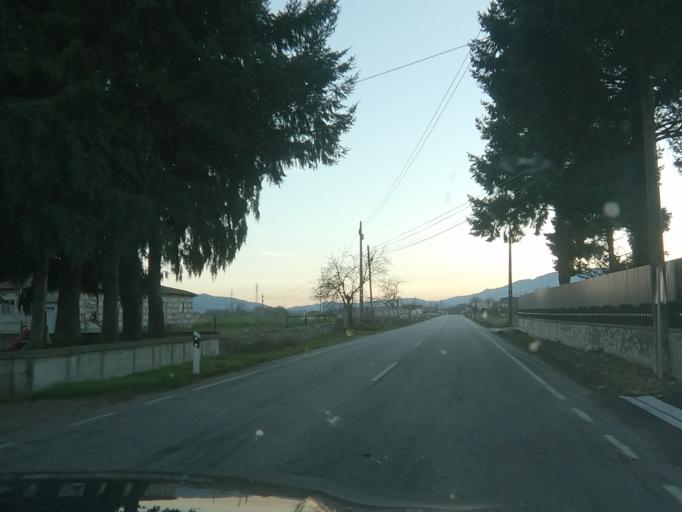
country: PT
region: Vila Real
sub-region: Vila Pouca de Aguiar
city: Vila Pouca de Aguiar
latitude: 41.4728
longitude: -7.6609
